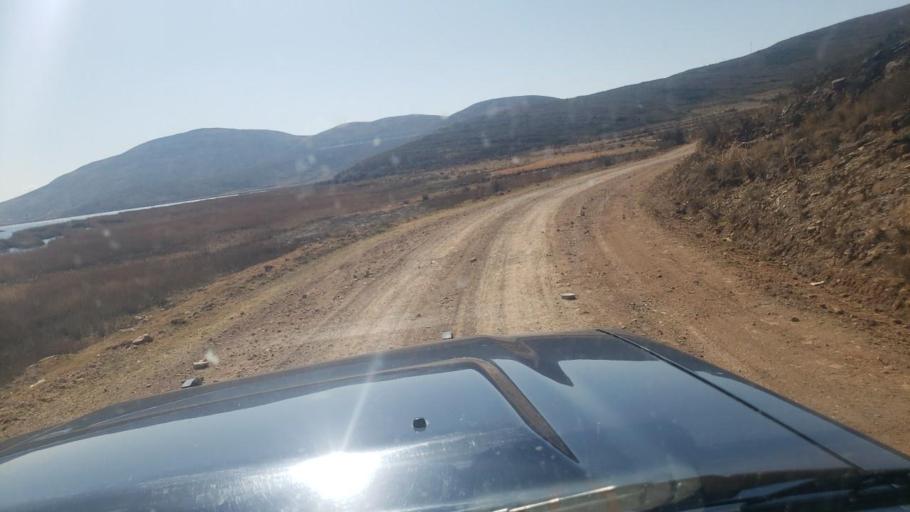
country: BO
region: La Paz
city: Huatajata
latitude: -16.3375
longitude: -68.6887
